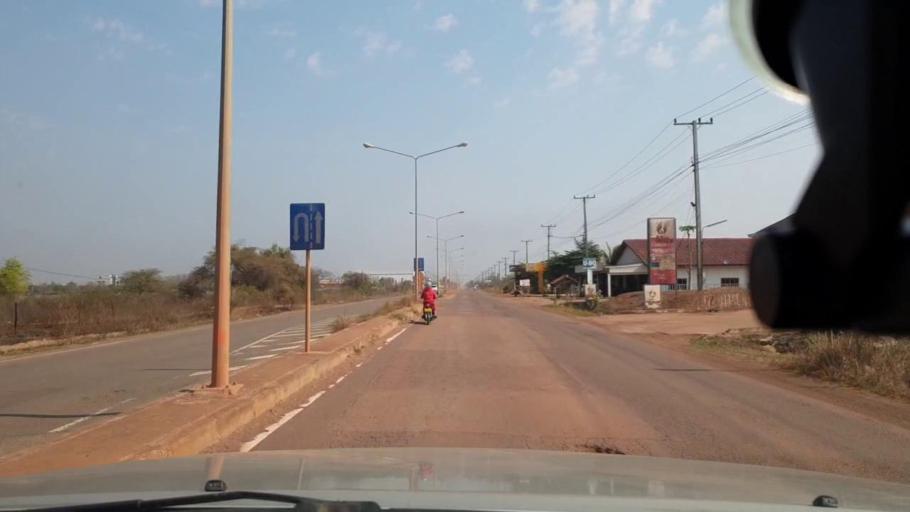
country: LA
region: Vientiane
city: Vientiane
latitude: 18.0050
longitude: 102.7198
